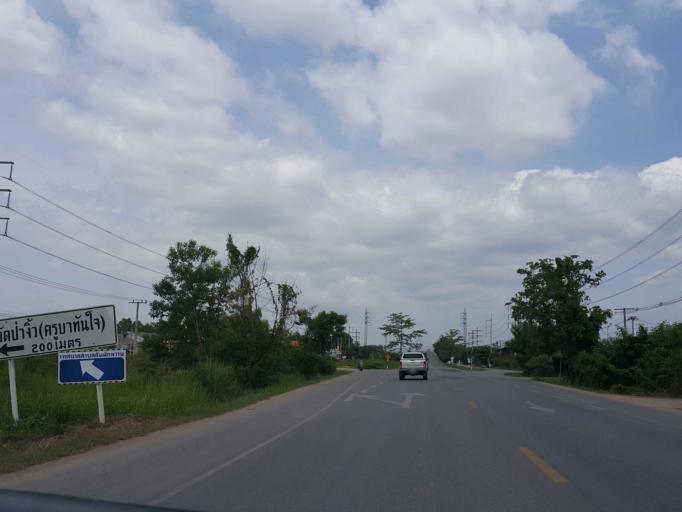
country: TH
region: Chiang Mai
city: Saraphi
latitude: 18.7200
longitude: 98.9931
